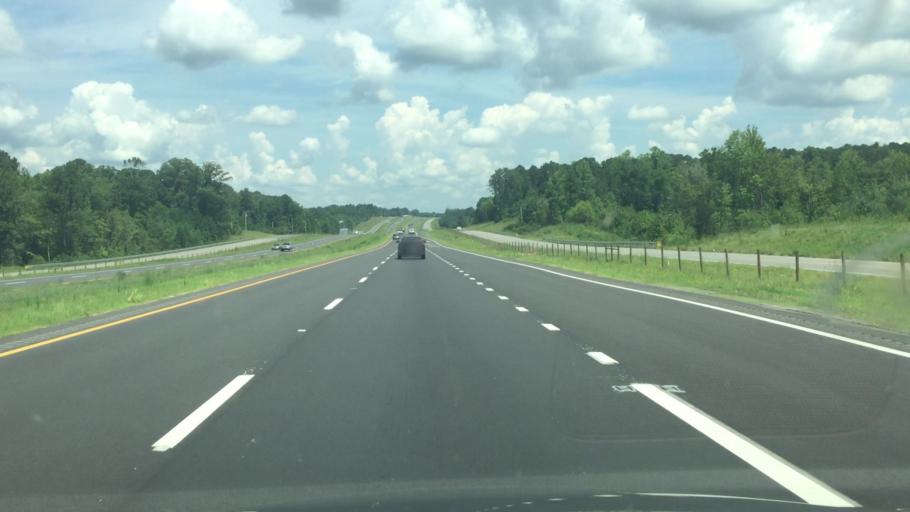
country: US
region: North Carolina
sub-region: Richmond County
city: Ellerbe
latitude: 35.0178
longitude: -79.7699
